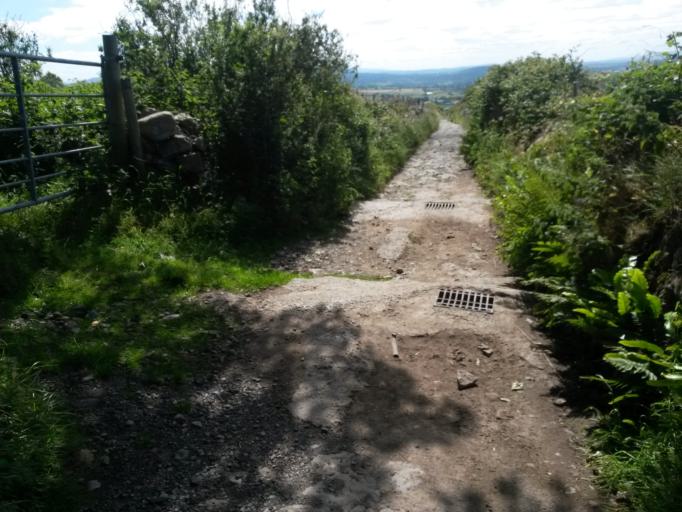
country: IE
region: Connaught
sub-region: Sligo
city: Strandhill
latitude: 54.2542
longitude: -8.5597
